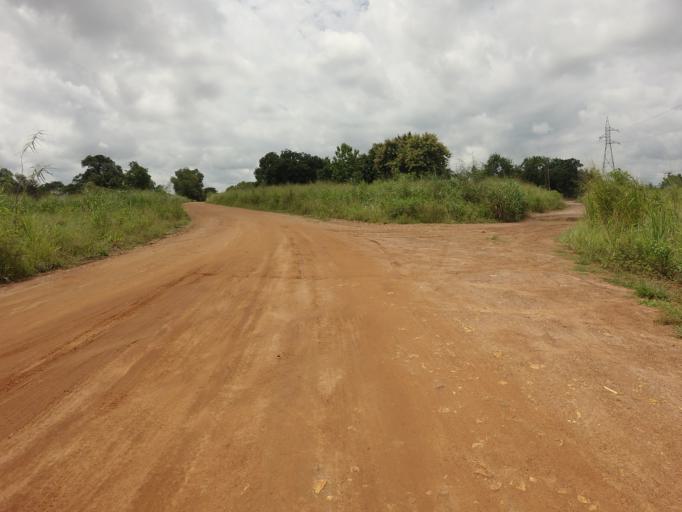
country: GH
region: Volta
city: Ho
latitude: 6.5880
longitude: 0.4681
